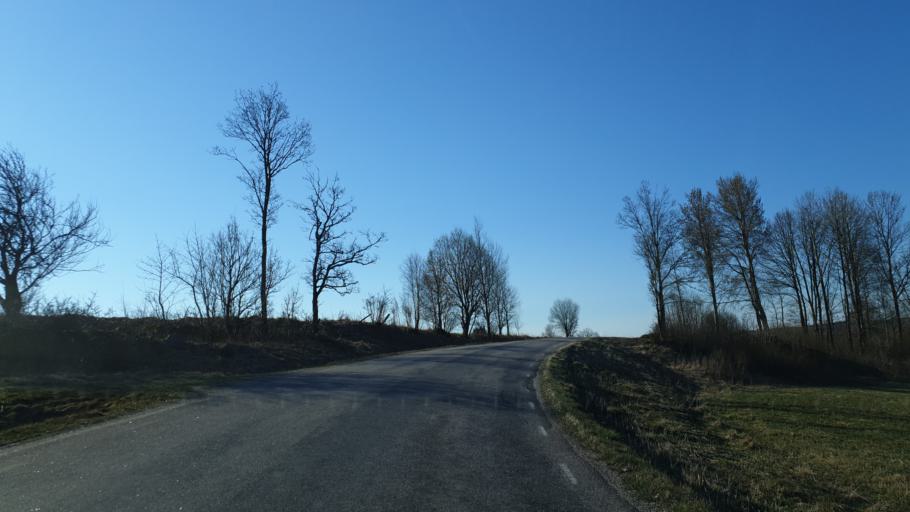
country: SE
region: Vaestra Goetaland
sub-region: Boras Kommun
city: Dalsjofors
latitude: 57.7780
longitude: 13.1012
